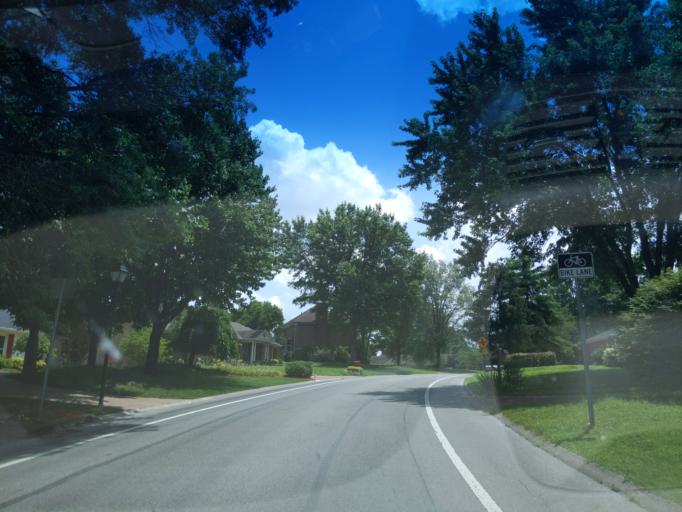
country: US
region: Tennessee
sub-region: Williamson County
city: Brentwood
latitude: 36.0423
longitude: -86.7617
